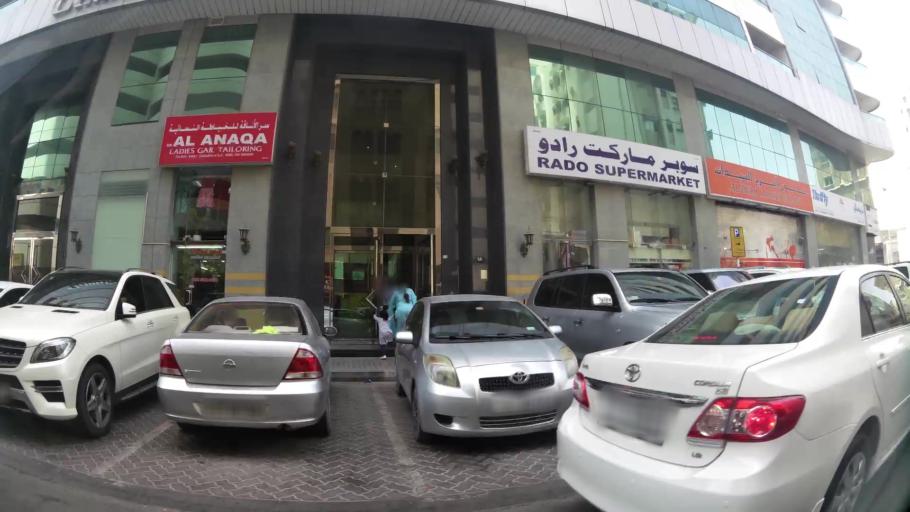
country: AE
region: Ash Shariqah
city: Sharjah
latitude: 25.3542
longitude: 55.3905
